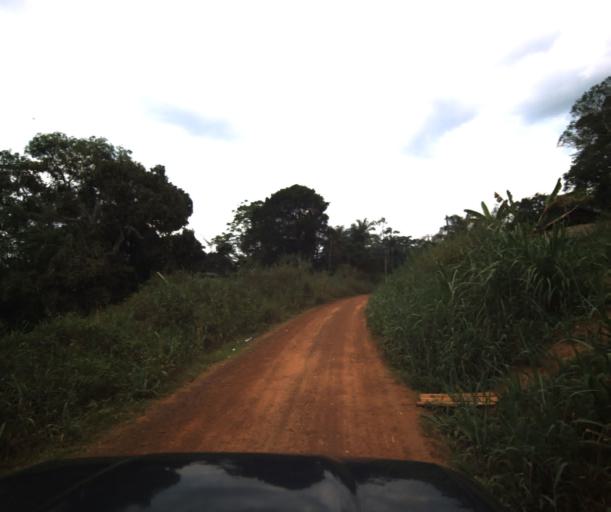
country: CM
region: Centre
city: Akono
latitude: 3.5944
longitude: 11.1631
